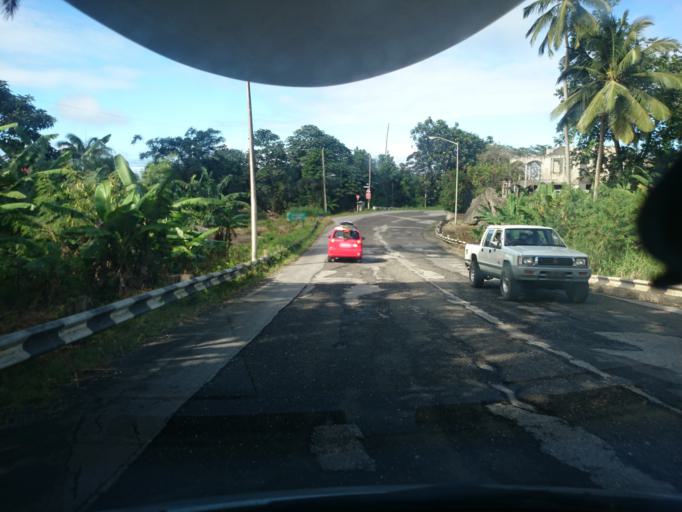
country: BB
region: Saint Joseph
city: Bathsheba
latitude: 13.2020
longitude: -59.5388
